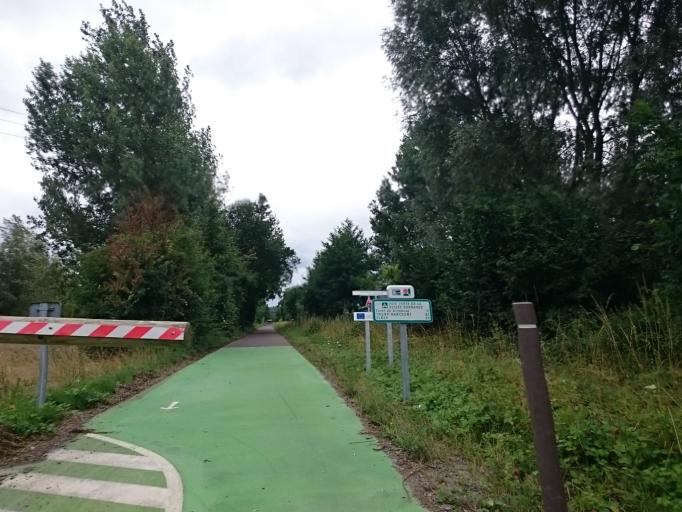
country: FR
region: Lower Normandy
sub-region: Departement du Calvados
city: Louvigny
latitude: 49.1380
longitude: -0.3950
